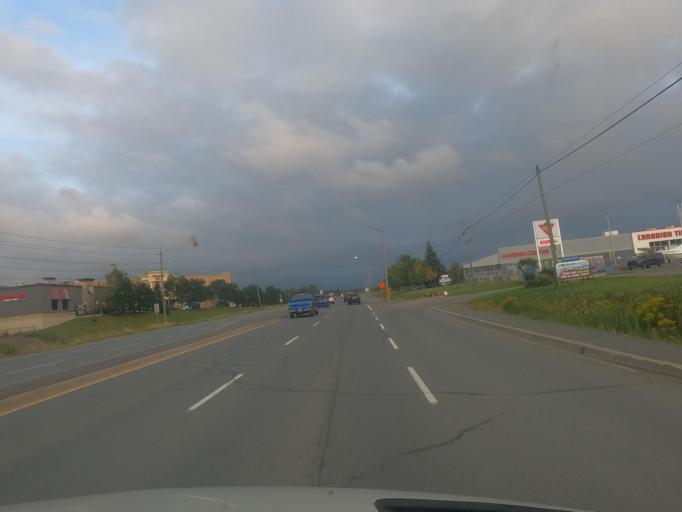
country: CA
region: Ontario
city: Greater Sudbury
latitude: 46.4489
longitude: -80.9938
